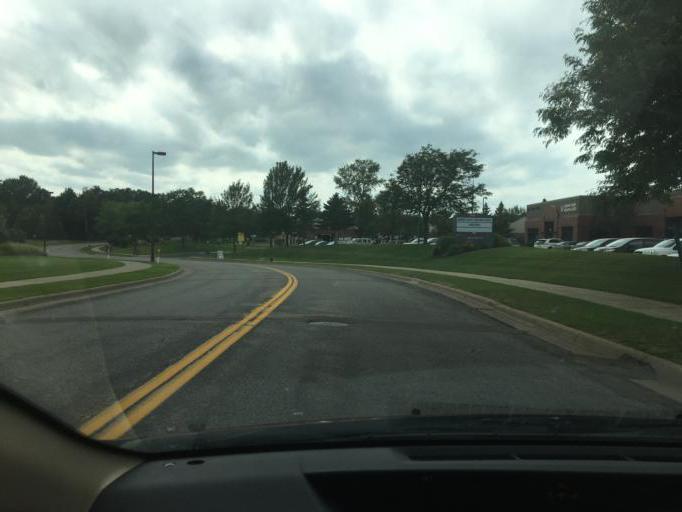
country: US
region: Minnesota
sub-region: Carver County
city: Chanhassen
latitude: 44.8610
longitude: -93.5193
